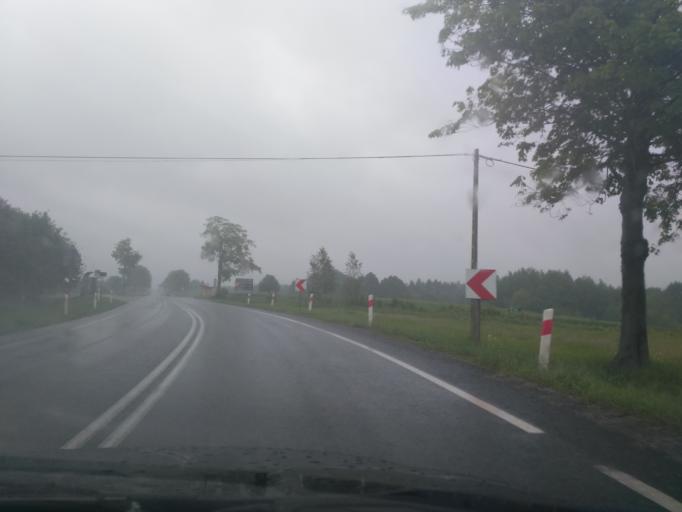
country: PL
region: Subcarpathian Voivodeship
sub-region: Powiat jasielski
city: Tarnowiec
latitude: 49.7639
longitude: 21.5752
